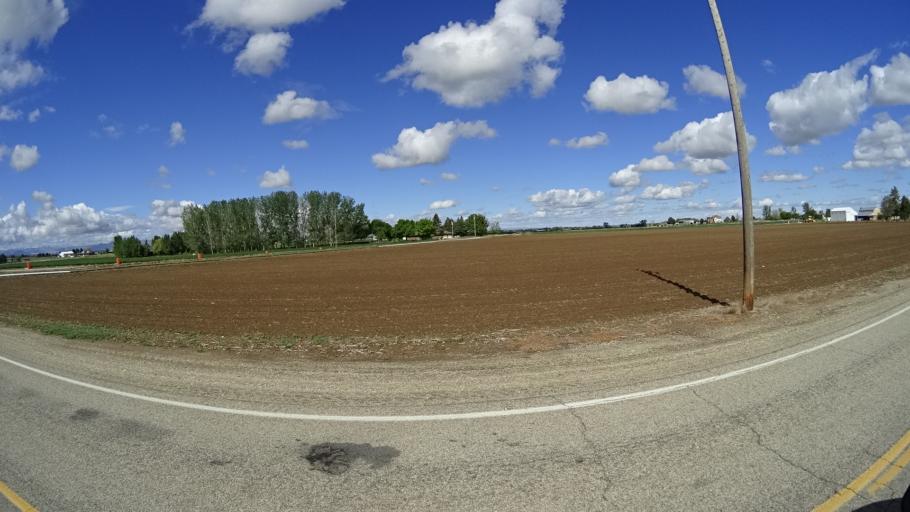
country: US
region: Idaho
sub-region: Ada County
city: Kuna
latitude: 43.4915
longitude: -116.4732
